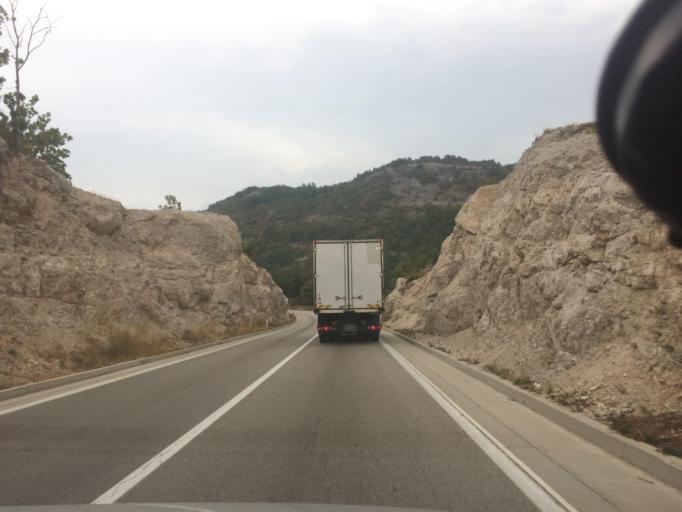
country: ME
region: Kotor
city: Risan
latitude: 42.6889
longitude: 18.6362
